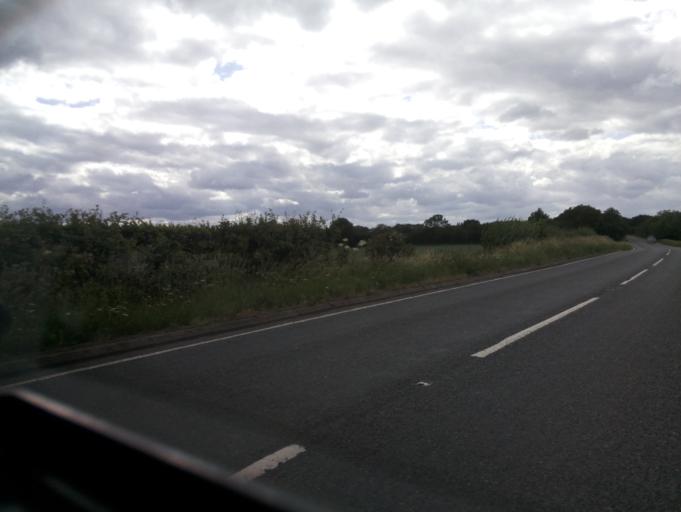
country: GB
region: England
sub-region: Leicestershire
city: Measham
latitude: 52.6516
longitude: -1.5156
